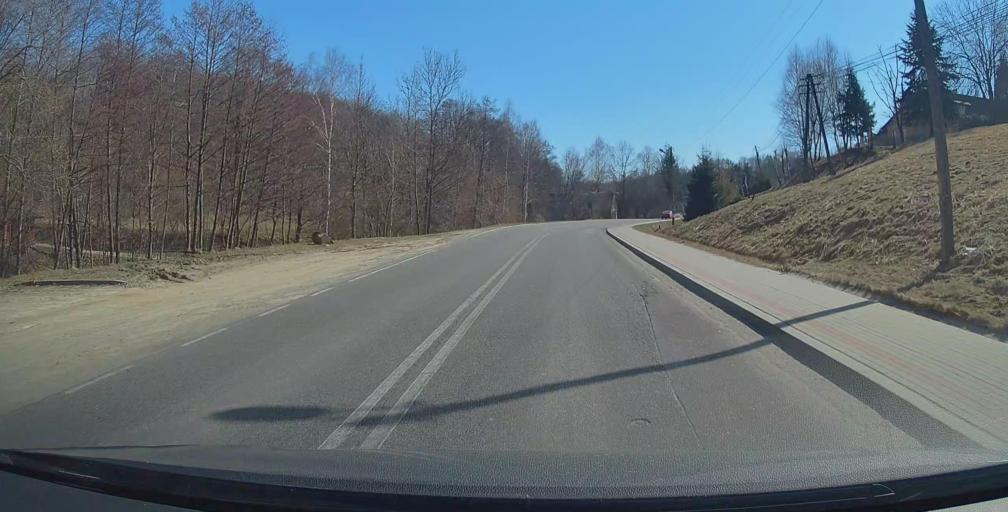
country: PL
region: Subcarpathian Voivodeship
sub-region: Powiat rzeszowski
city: Hyzne
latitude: 49.9049
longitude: 22.2079
